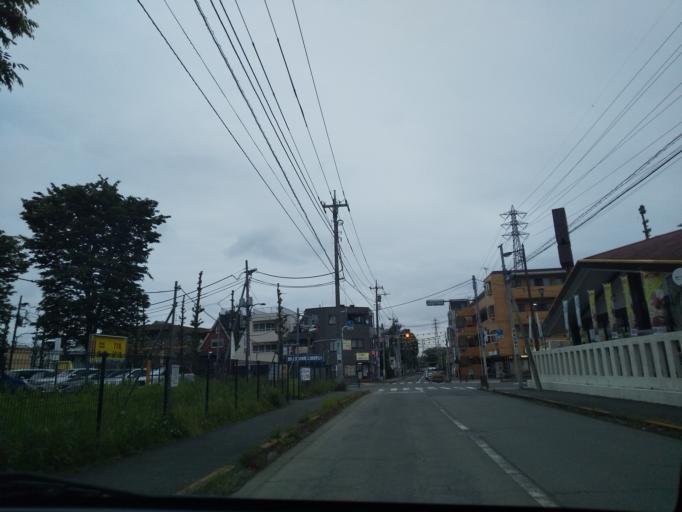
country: JP
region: Tokyo
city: Hino
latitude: 35.6637
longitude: 139.3787
